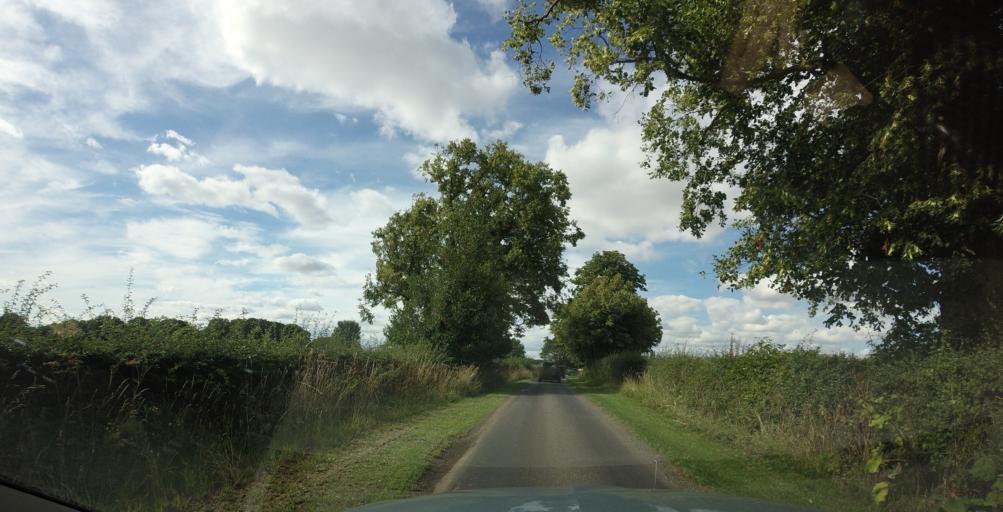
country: GB
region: England
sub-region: North Yorkshire
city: Ripon
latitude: 54.1150
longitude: -1.4821
